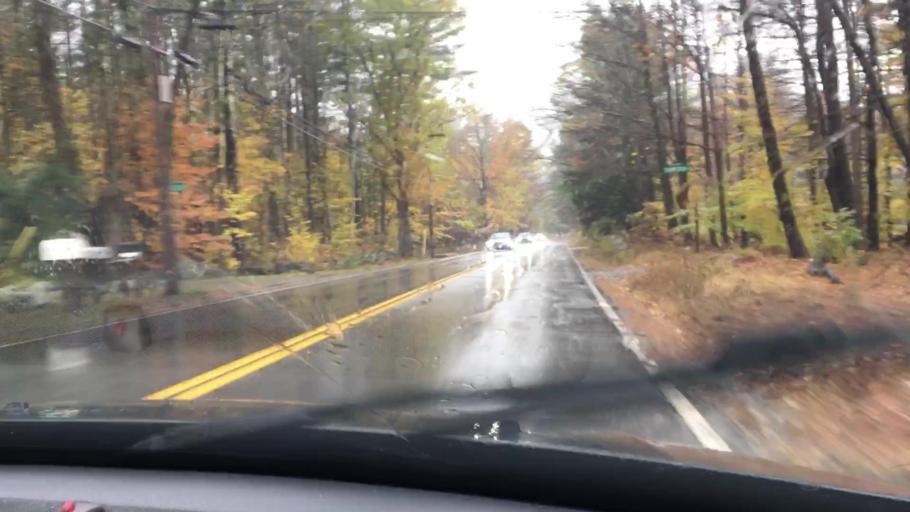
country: US
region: New Hampshire
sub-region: Grafton County
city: Holderness
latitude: 43.7222
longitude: -71.5556
